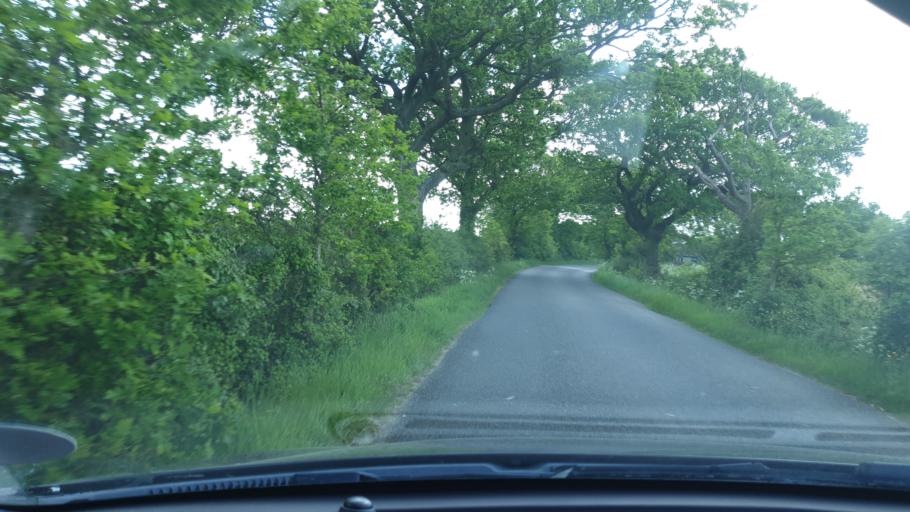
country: GB
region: England
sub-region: Essex
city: Great Bentley
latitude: 51.8470
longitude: 1.0898
